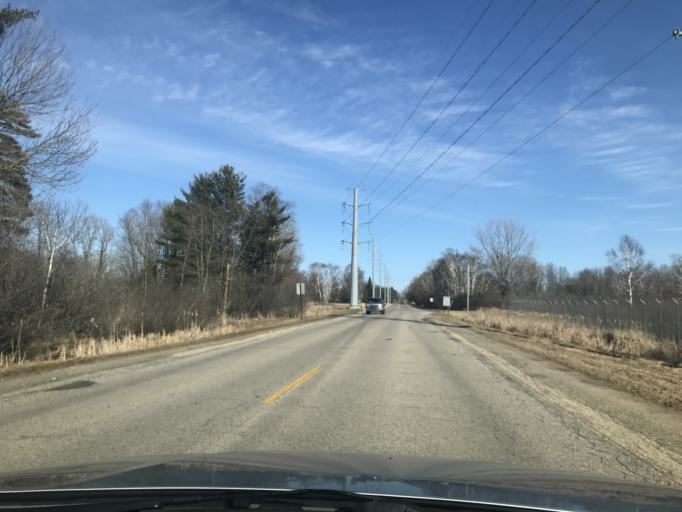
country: US
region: Michigan
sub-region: Menominee County
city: Menominee
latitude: 45.1445
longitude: -87.6241
